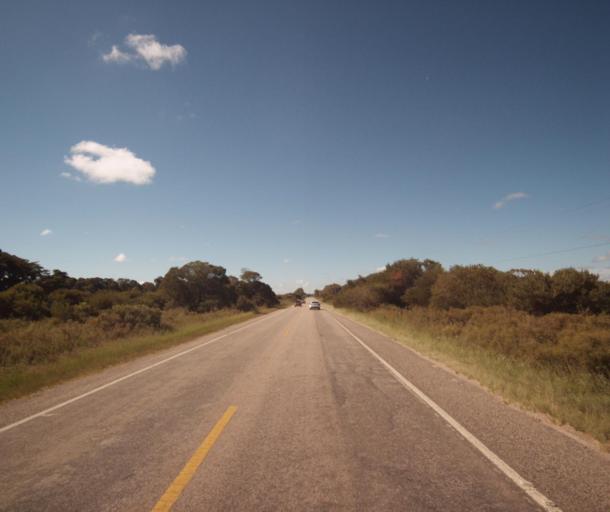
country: BR
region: Rio Grande do Sul
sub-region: Santa Vitoria Do Palmar
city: Santa Vitoria do Palmar
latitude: -33.5735
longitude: -53.3765
